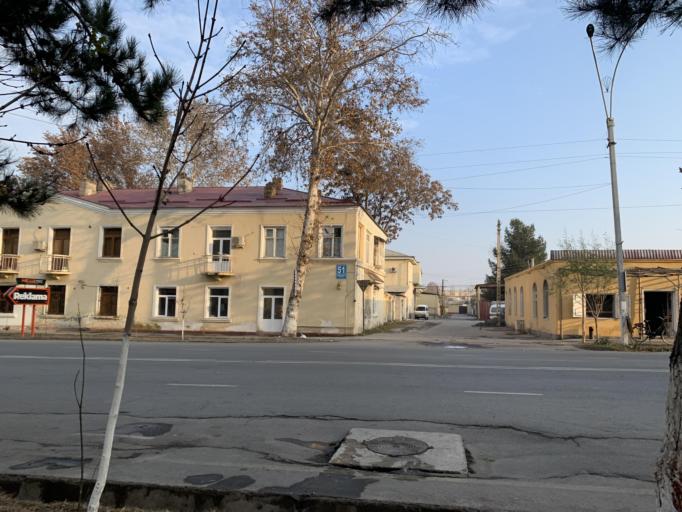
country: UZ
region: Fergana
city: Qo`qon
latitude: 40.5413
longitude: 70.9233
